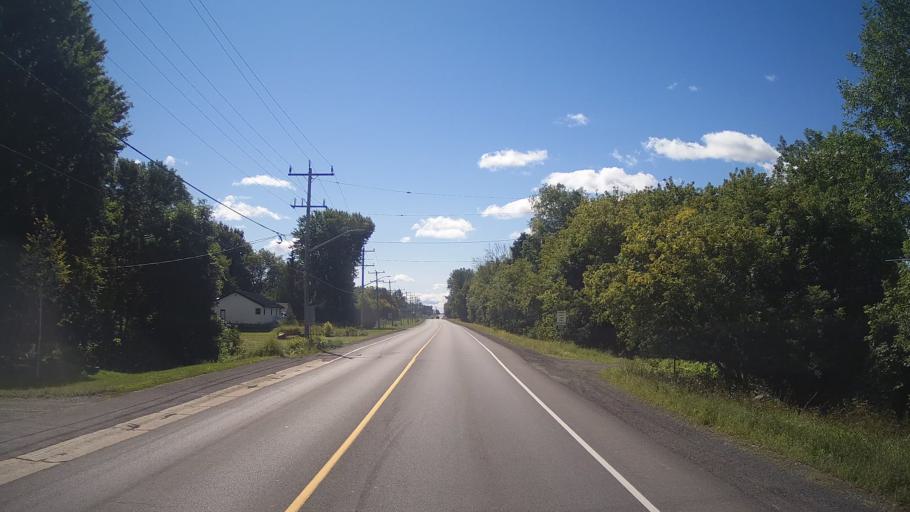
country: US
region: New York
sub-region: St. Lawrence County
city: Norfolk
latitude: 44.9713
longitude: -75.2409
